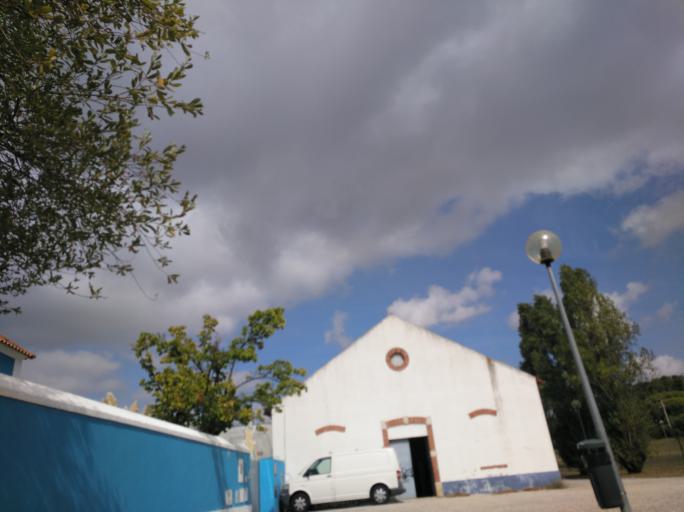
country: PT
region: Lisbon
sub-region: Lisbon
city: Lisbon
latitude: 38.7455
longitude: -9.1249
